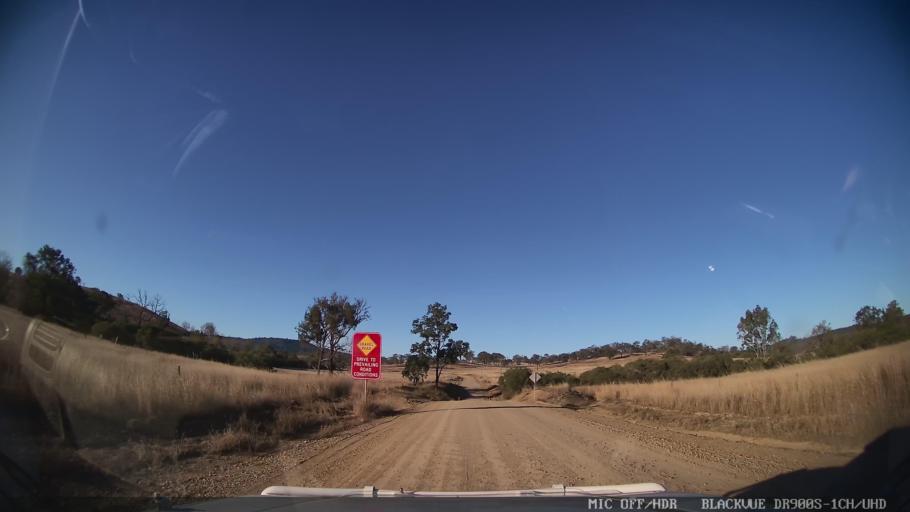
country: AU
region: Queensland
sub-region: Gladstone
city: Toolooa
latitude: -24.6897
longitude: 151.3068
